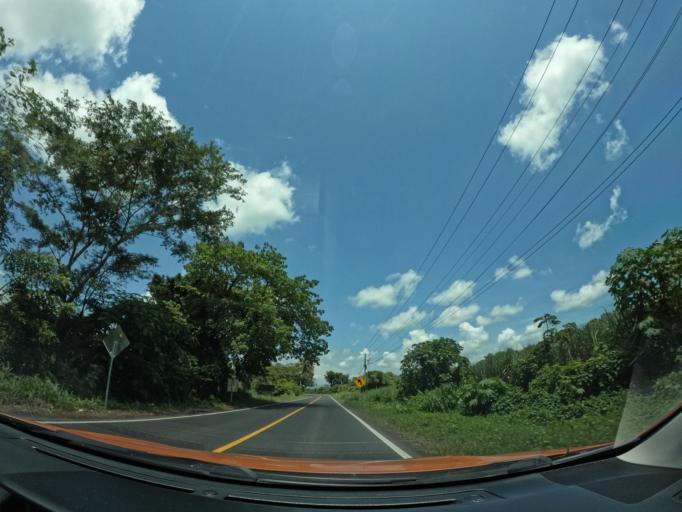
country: GT
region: Escuintla
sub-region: Municipio de Masagua
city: Masagua
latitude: 14.1554
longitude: -90.8811
